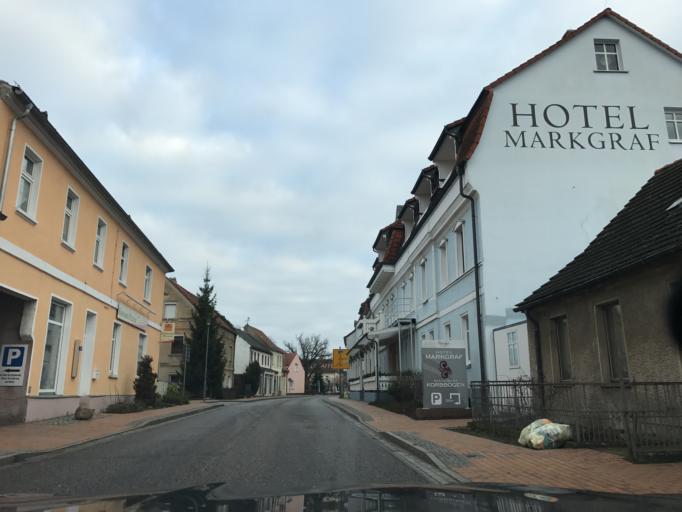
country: DE
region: Brandenburg
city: Gross Kreutz
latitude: 52.3179
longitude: 12.7433
